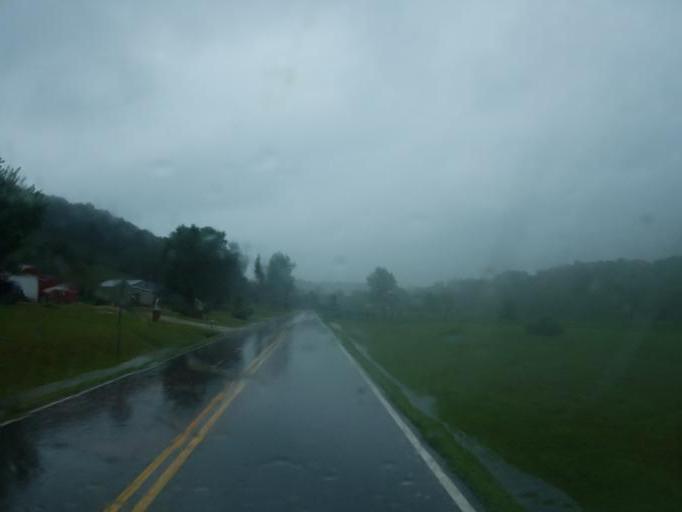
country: US
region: Kentucky
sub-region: Carter County
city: Grayson
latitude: 38.4750
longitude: -83.0339
